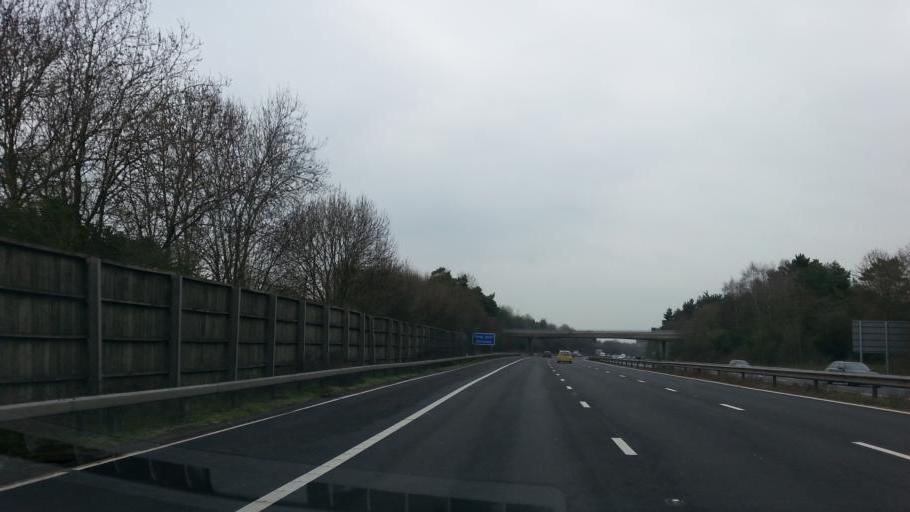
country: GB
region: England
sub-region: Gloucestershire
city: Barnwood
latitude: 51.8337
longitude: -2.2041
